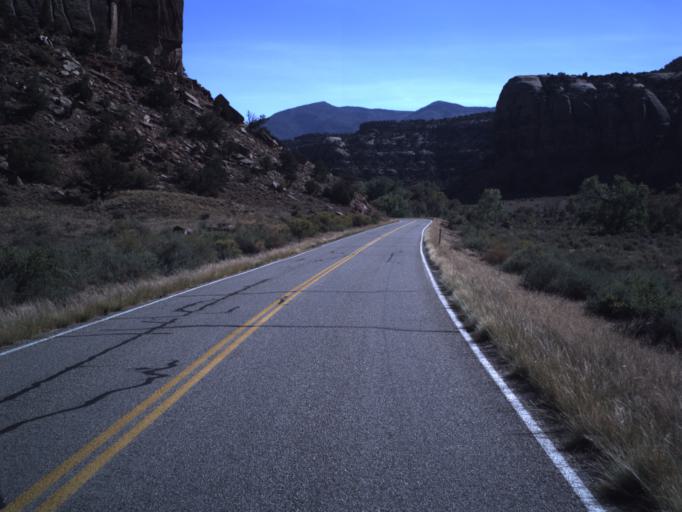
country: US
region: Utah
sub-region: San Juan County
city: Monticello
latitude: 38.0300
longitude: -109.5410
